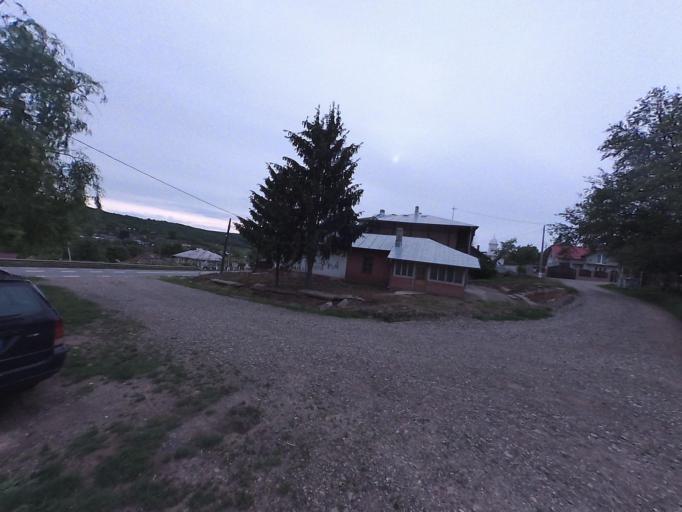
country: RO
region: Neamt
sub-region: Comuna Dulcesti
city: Dulcesti
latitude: 46.9661
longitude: 26.7868
